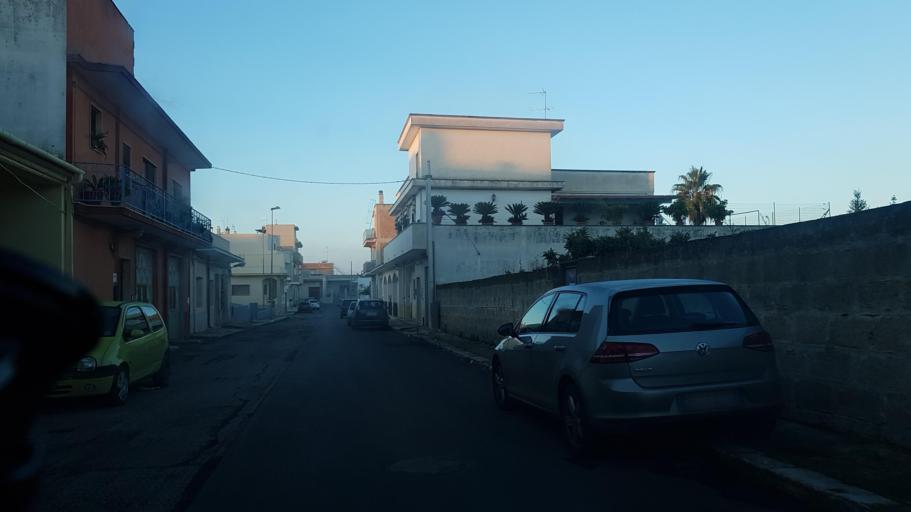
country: IT
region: Apulia
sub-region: Provincia di Brindisi
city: San Michele Salentino
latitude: 40.6307
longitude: 17.6368
